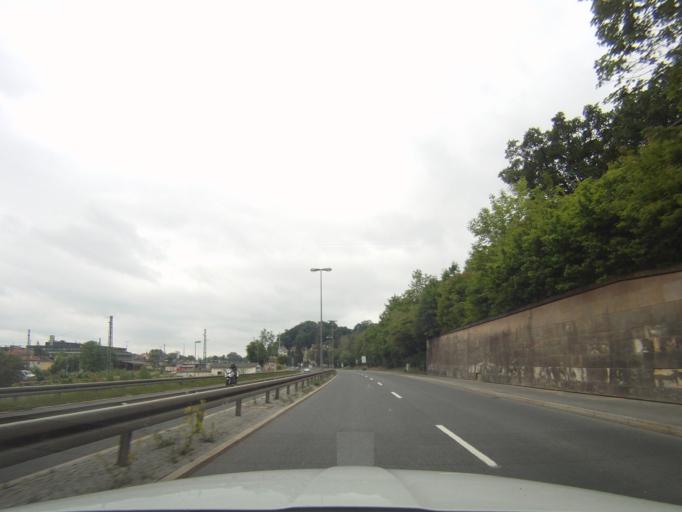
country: DE
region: Bavaria
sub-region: Upper Franconia
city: Coburg
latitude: 50.2661
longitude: 10.9557
